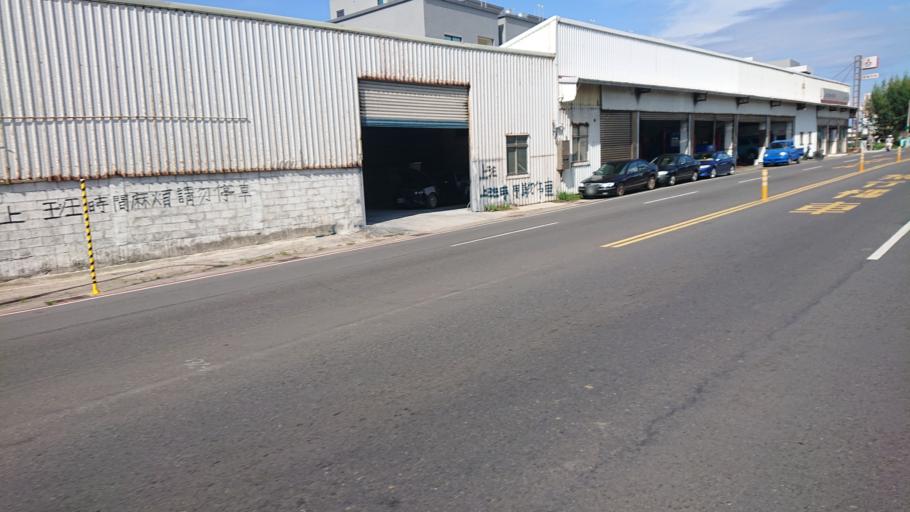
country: TW
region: Taiwan
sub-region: Penghu
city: Ma-kung
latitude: 23.5626
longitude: 119.5918
